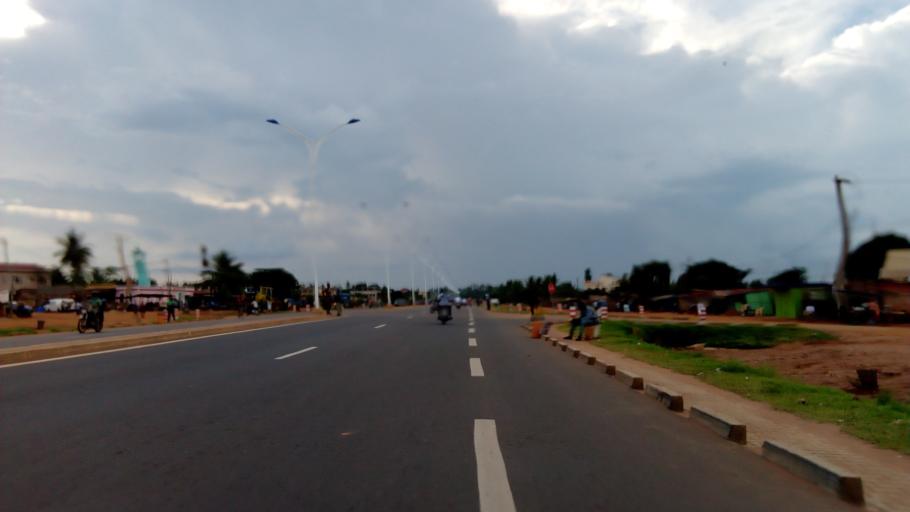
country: TG
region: Maritime
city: Lome
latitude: 6.2424
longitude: 1.1993
